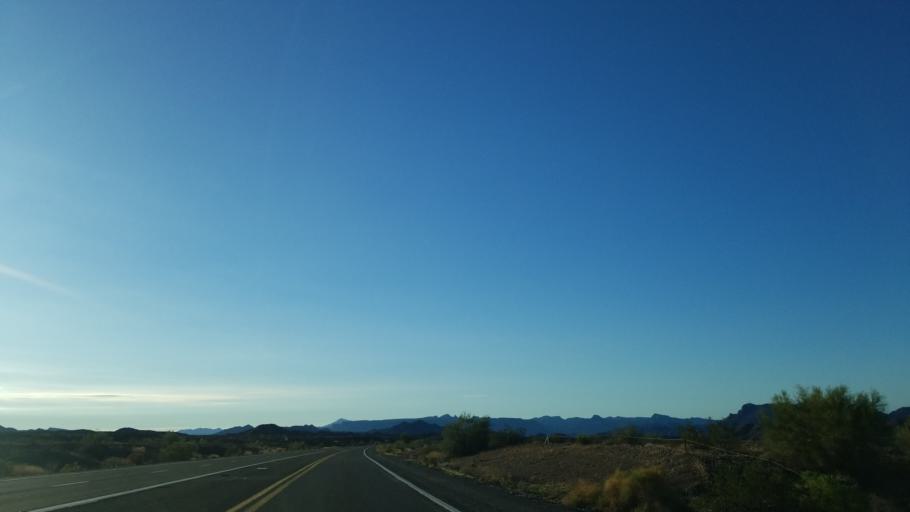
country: US
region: Arizona
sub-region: Mohave County
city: Lake Havasu City
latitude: 34.3916
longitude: -114.1717
